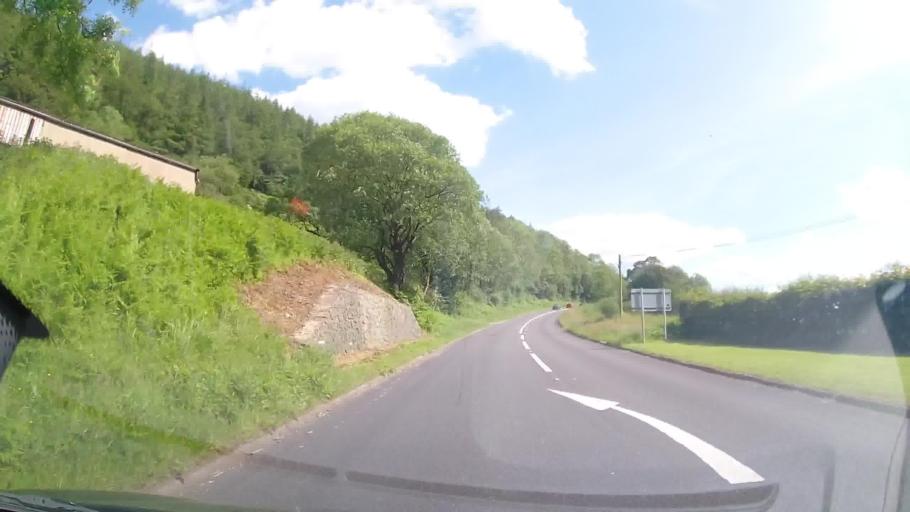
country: GB
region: Wales
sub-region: Gwynedd
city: Corris
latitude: 52.7093
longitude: -3.6871
